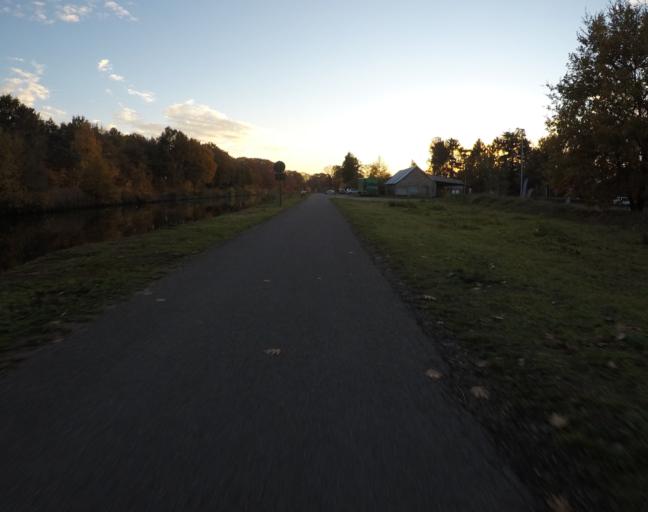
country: BE
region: Flanders
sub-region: Provincie Antwerpen
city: Herentals
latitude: 51.1749
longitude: 4.8549
